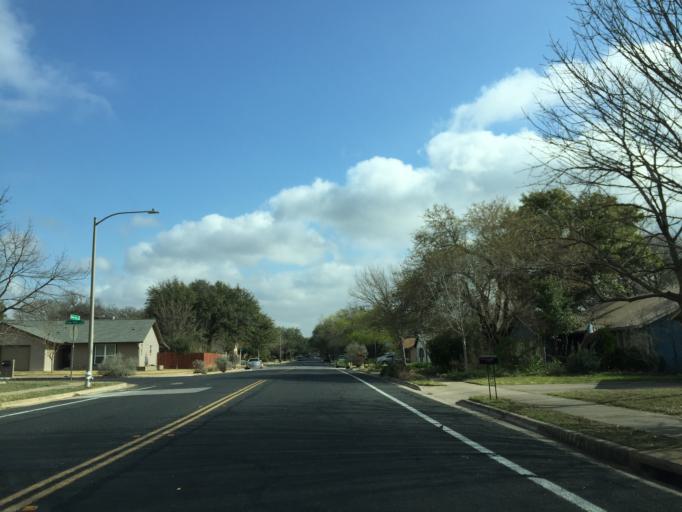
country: US
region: Texas
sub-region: Williamson County
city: Jollyville
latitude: 30.4101
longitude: -97.7365
